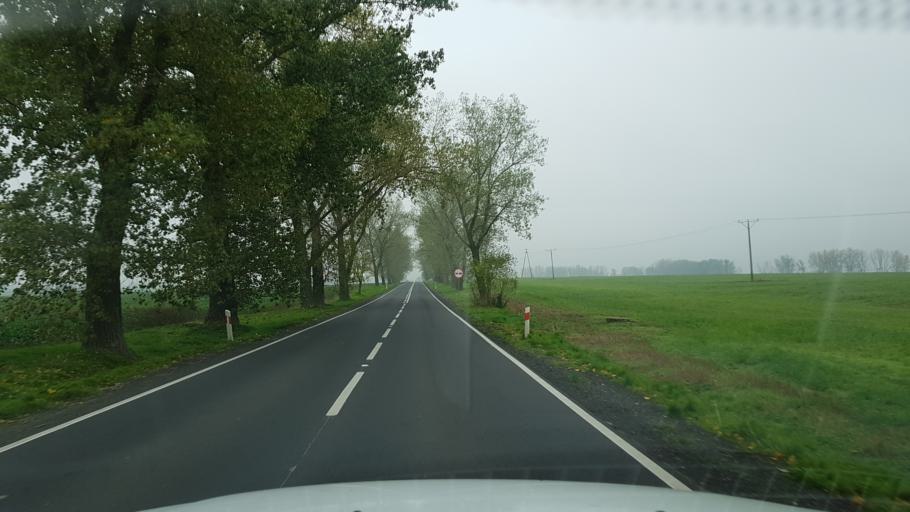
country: PL
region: West Pomeranian Voivodeship
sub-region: Powiat stargardzki
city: Stargard Szczecinski
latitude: 53.2522
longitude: 15.1018
